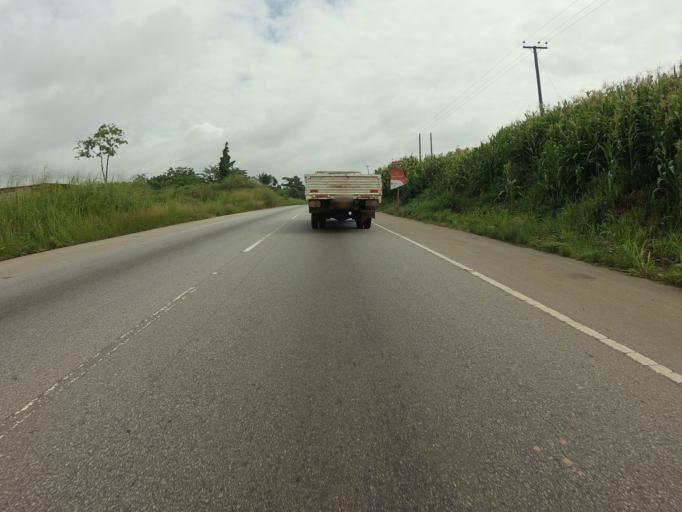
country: GH
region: Ashanti
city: Tafo
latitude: 6.9857
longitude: -1.6890
